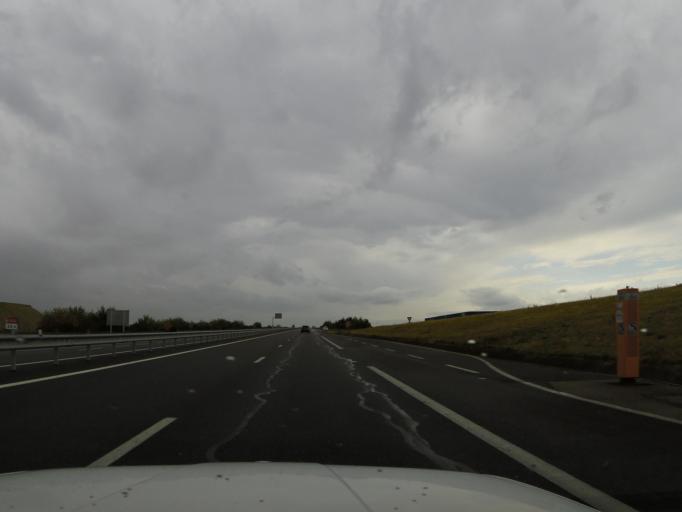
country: FR
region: Rhone-Alpes
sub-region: Departement du Rhone
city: Pusignan
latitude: 45.7654
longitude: 5.0859
